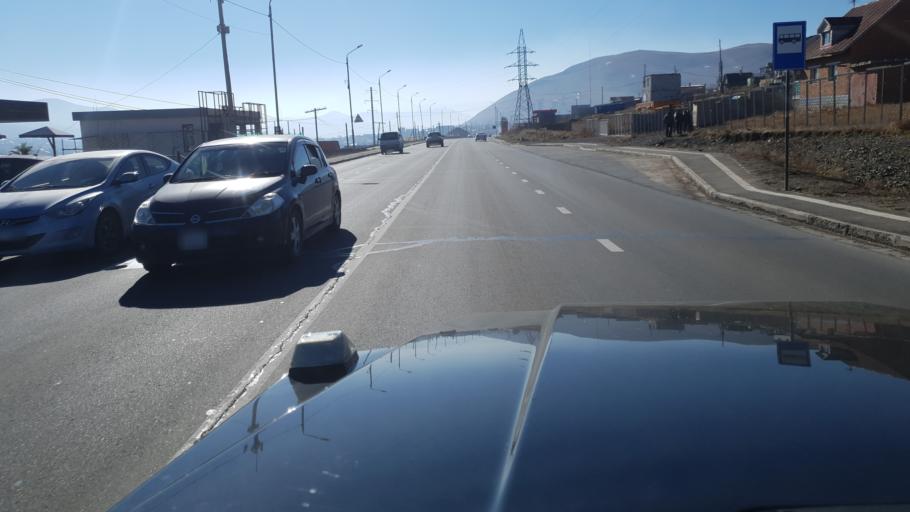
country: MN
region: Ulaanbaatar
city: Ulaanbaatar
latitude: 48.0253
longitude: 106.9132
